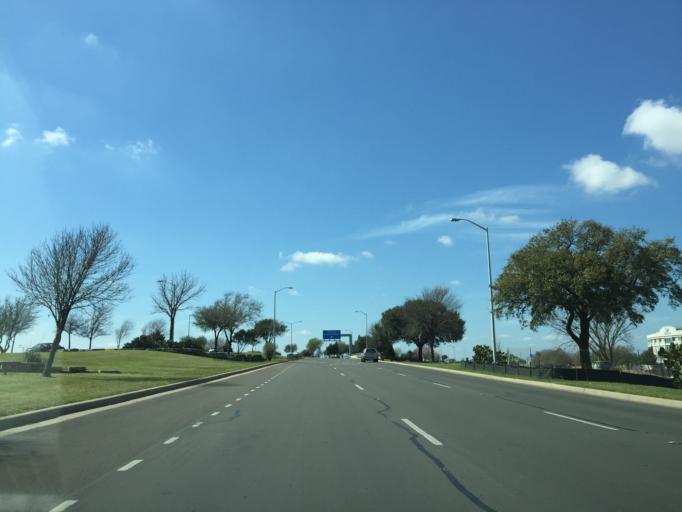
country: US
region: Texas
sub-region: Travis County
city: Hornsby Bend
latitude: 30.2117
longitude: -97.6603
